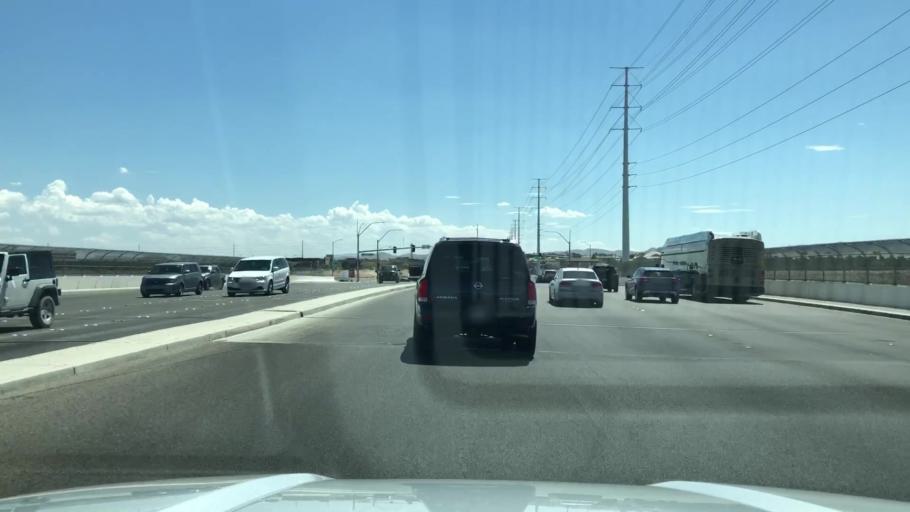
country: US
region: Nevada
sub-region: Clark County
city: Spring Valley
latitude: 36.0667
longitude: -115.2795
